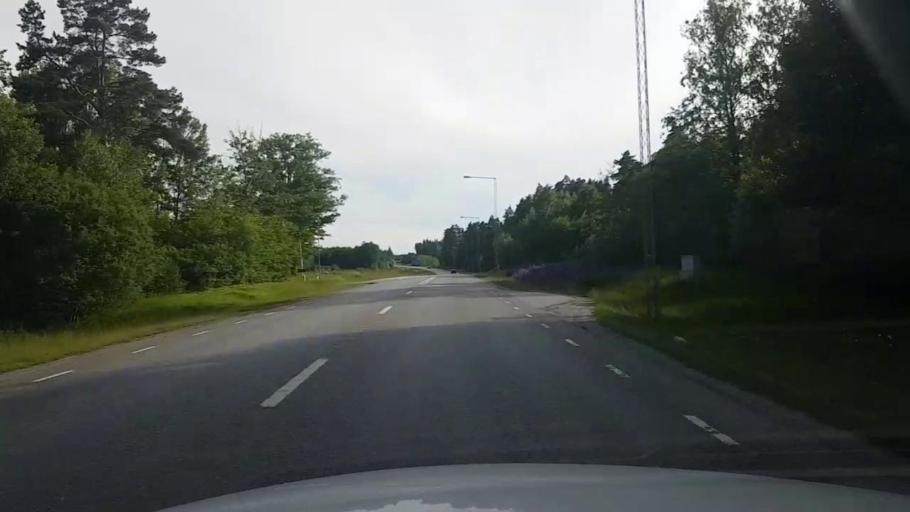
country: SE
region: Stockholm
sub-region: Sigtuna Kommun
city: Rosersberg
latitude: 59.6349
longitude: 17.9337
